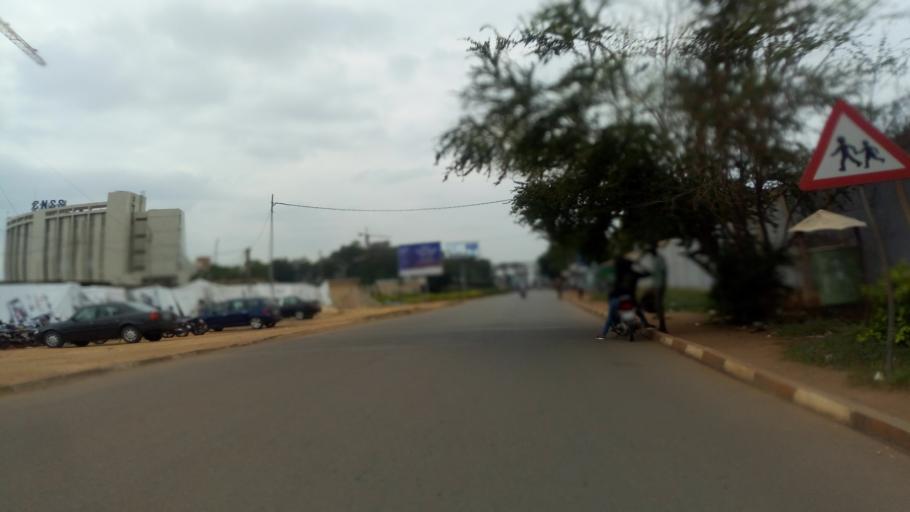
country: TG
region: Maritime
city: Lome
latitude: 6.1874
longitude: 1.2088
